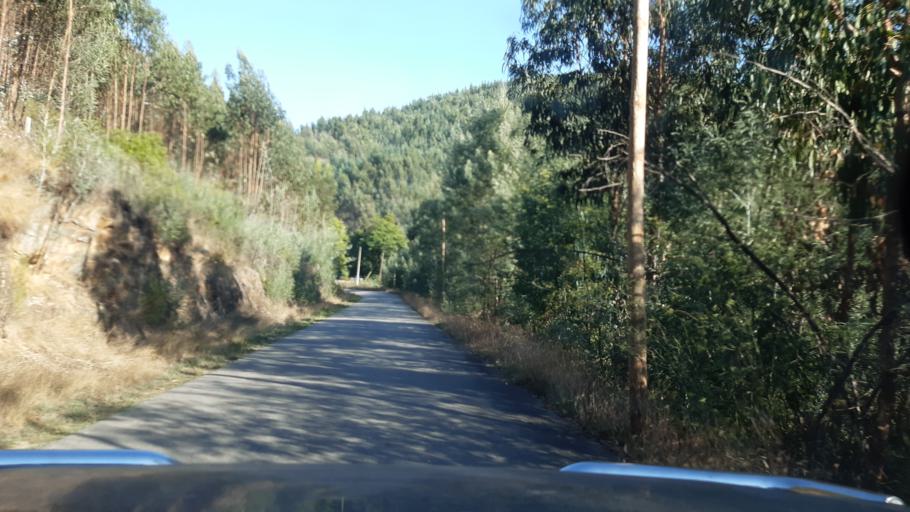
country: PT
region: Aveiro
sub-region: Agueda
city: Aguada de Cima
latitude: 40.5686
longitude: -8.3587
